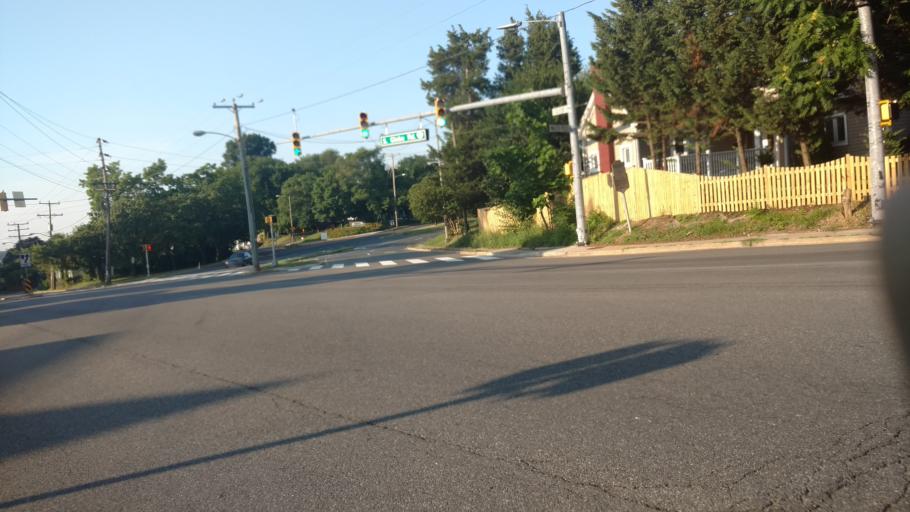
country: US
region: Virginia
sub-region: Arlington County
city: Arlington
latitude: 38.8554
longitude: -77.0886
